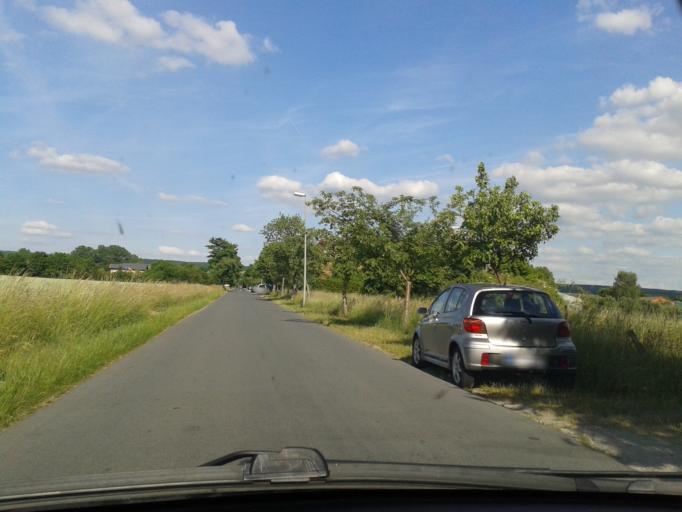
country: DE
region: North Rhine-Westphalia
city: Bad Lippspringe
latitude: 51.7830
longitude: 8.8320
